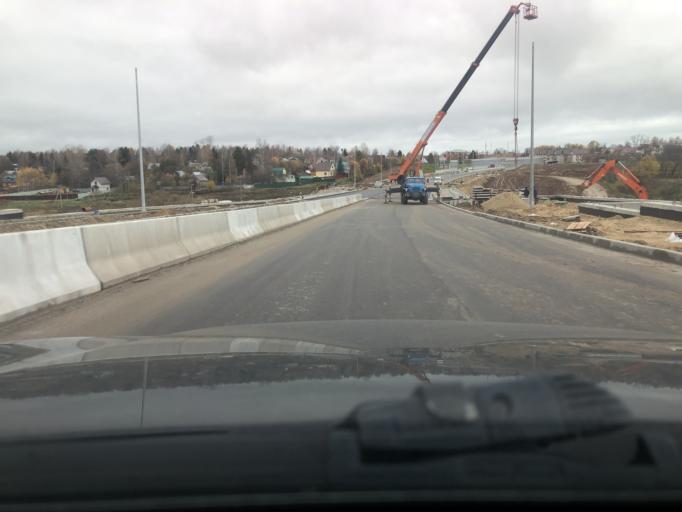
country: RU
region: Moskovskaya
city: Sergiyev Posad
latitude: 56.2992
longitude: 38.1005
